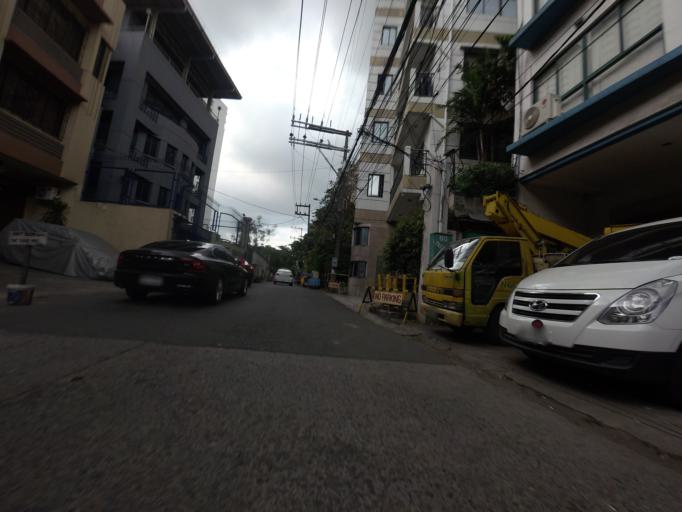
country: PH
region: Metro Manila
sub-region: City of Manila
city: Port Area
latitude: 14.5603
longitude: 120.9944
